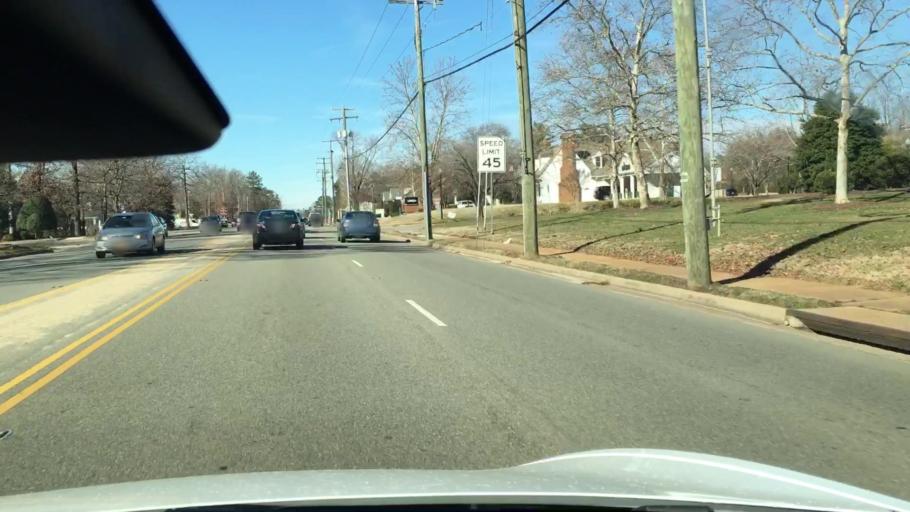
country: US
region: Virginia
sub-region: Chesterfield County
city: Brandermill
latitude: 37.5039
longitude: -77.6527
